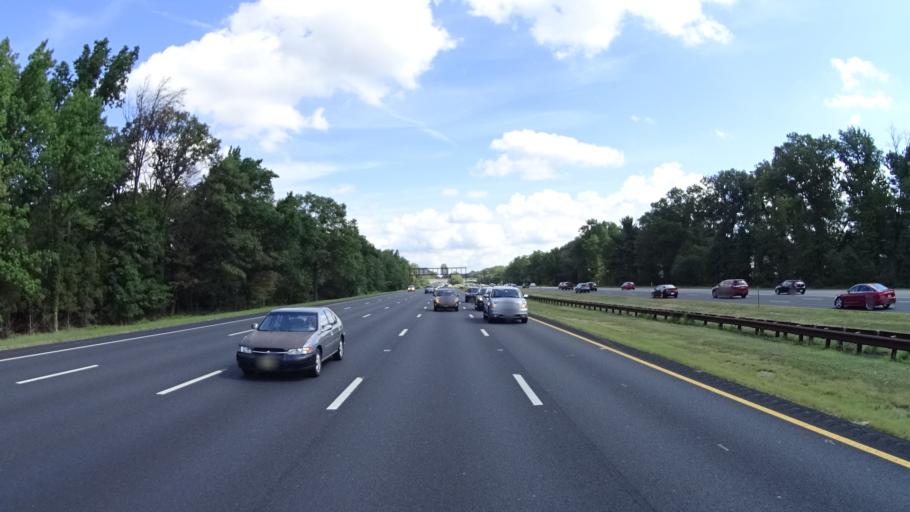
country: US
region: New Jersey
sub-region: Middlesex County
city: Iselin
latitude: 40.5937
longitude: -74.3228
